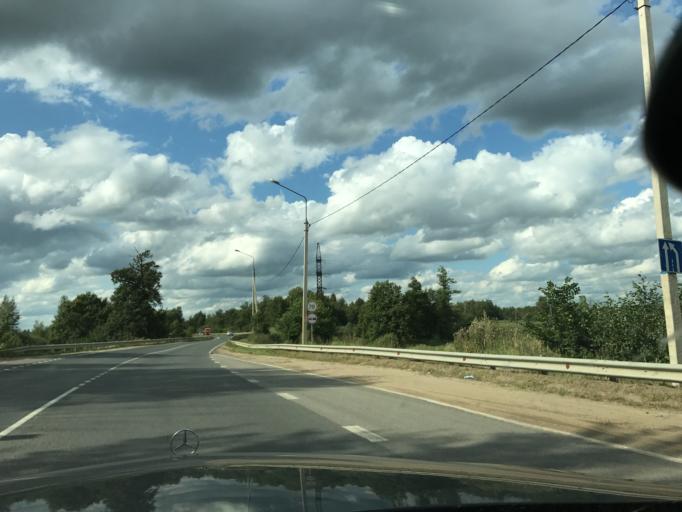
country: RU
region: Vladimir
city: Sobinka
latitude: 56.0007
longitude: 40.0112
